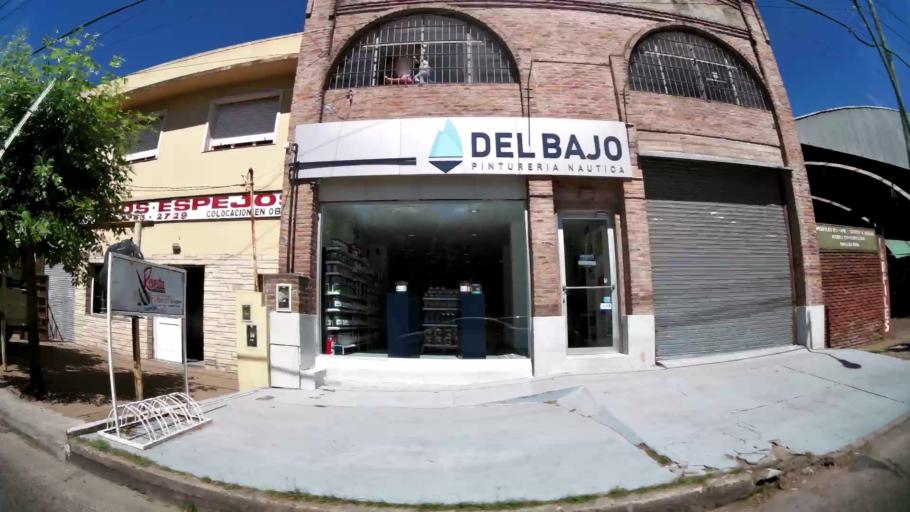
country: AR
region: Buenos Aires
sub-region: Partido de San Isidro
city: San Isidro
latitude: -34.4634
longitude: -58.5079
